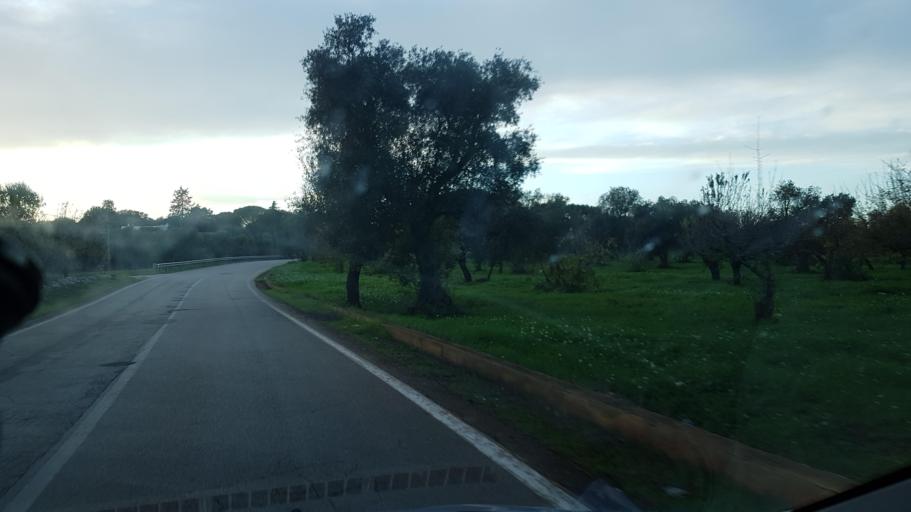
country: IT
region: Apulia
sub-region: Provincia di Brindisi
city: San Michele Salentino
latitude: 40.6410
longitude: 17.5814
